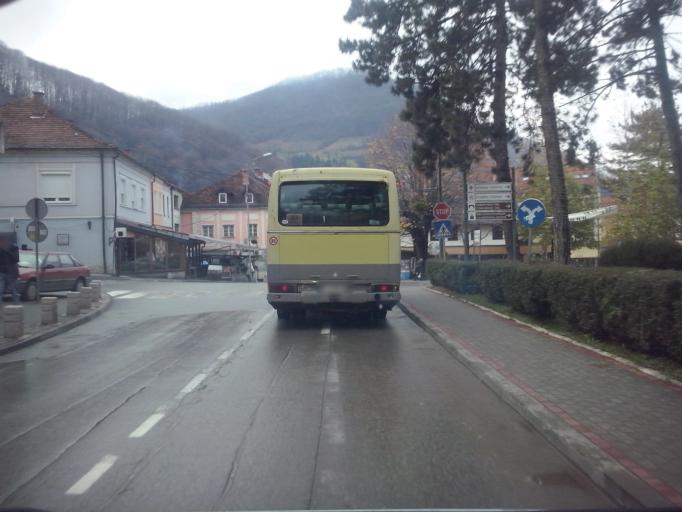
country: RS
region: Central Serbia
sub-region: Moravicki Okrug
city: Ivanjica
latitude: 43.5808
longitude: 20.2289
